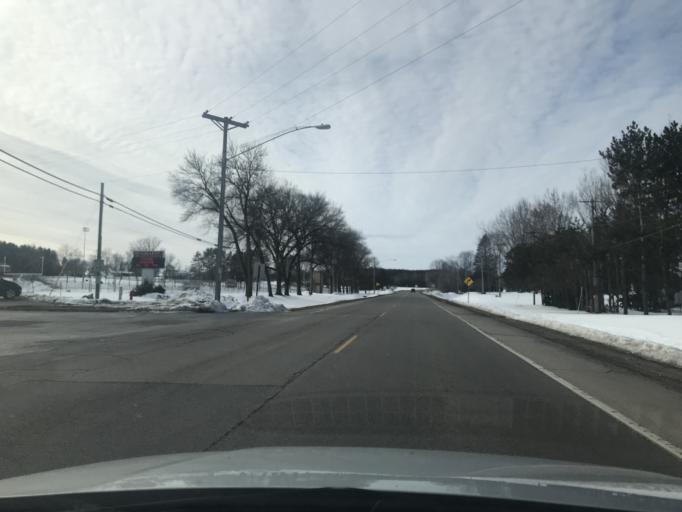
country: US
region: Wisconsin
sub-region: Oconto County
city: Gillett
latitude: 44.8875
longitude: -88.3151
